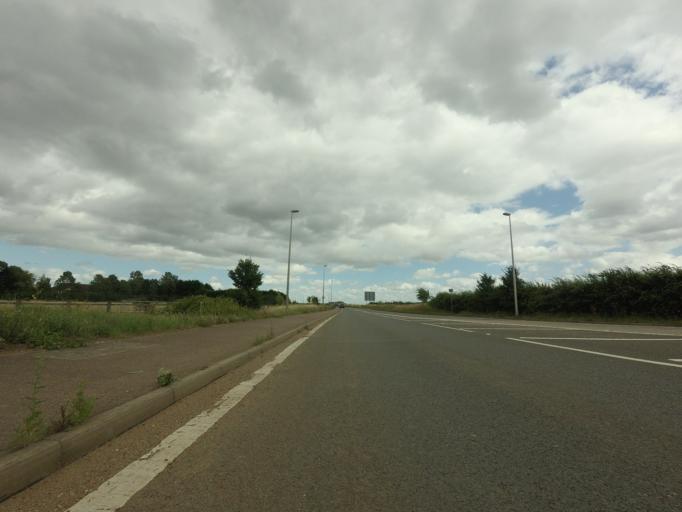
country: GB
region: England
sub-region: Medway
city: High Halstow
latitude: 51.4497
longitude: 0.5876
